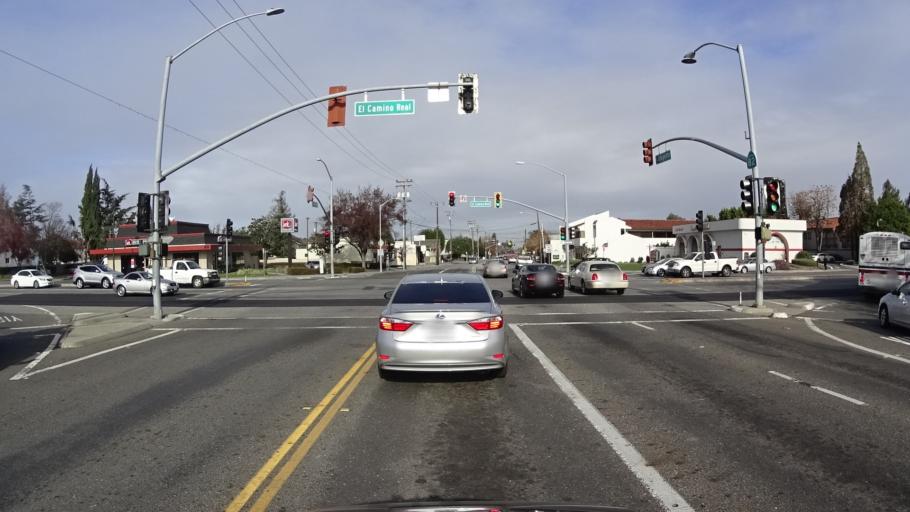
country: US
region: California
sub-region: Santa Clara County
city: Santa Clara
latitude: 37.3546
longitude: -121.9459
